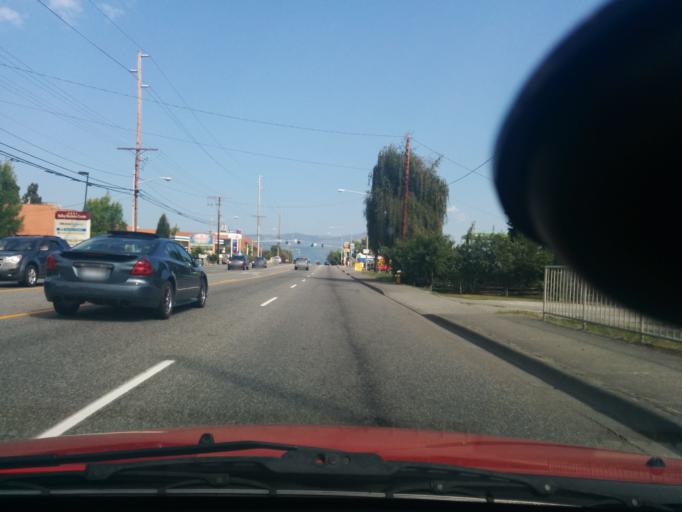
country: US
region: Washington
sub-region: Skagit County
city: Mount Vernon
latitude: 48.4356
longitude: -122.3160
